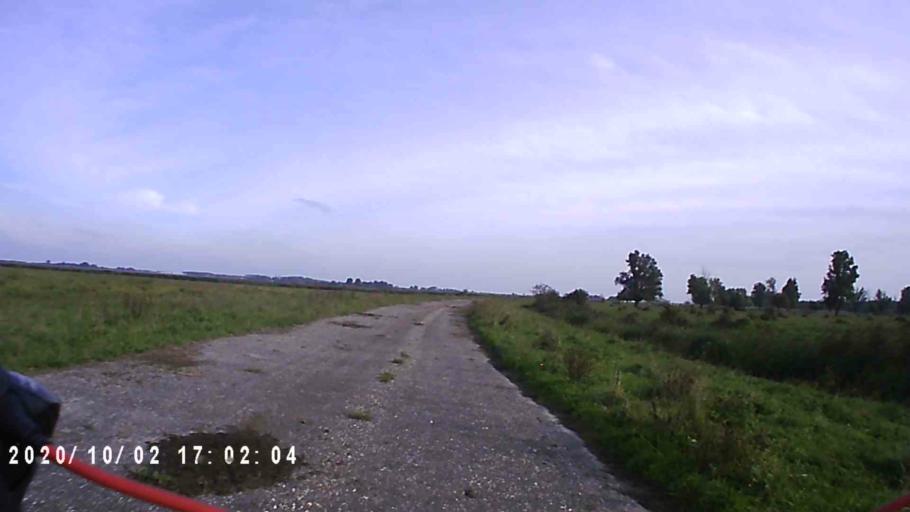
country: NL
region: Groningen
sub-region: Gemeente De Marne
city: Ulrum
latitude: 53.3429
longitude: 6.2614
